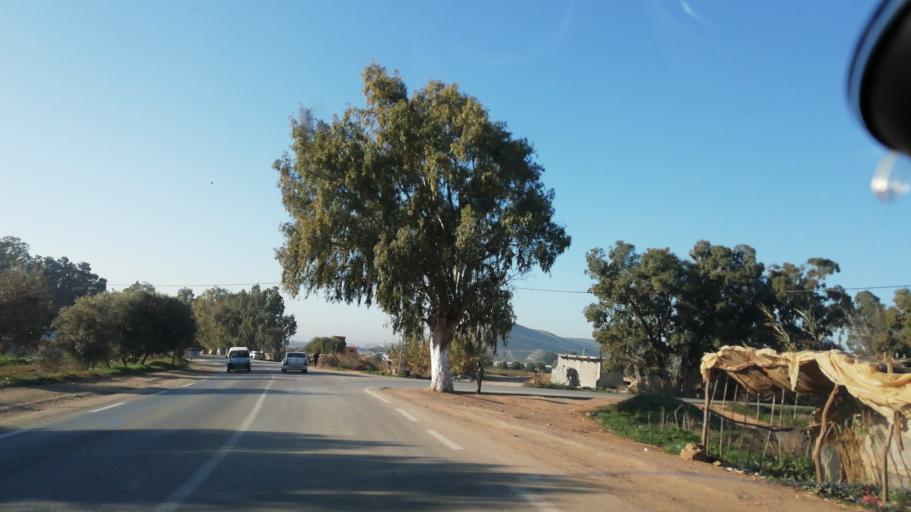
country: DZ
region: Tlemcen
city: Remchi
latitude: 35.0548
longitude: -1.5010
